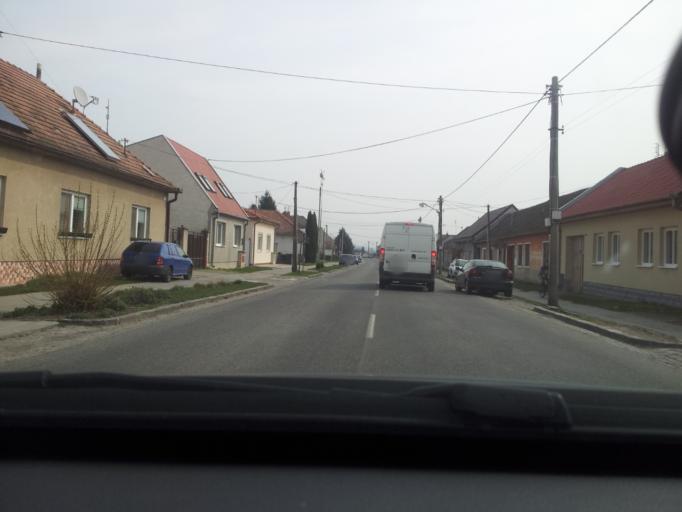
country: SK
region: Trnavsky
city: Leopoldov
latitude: 48.4396
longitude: 17.7106
